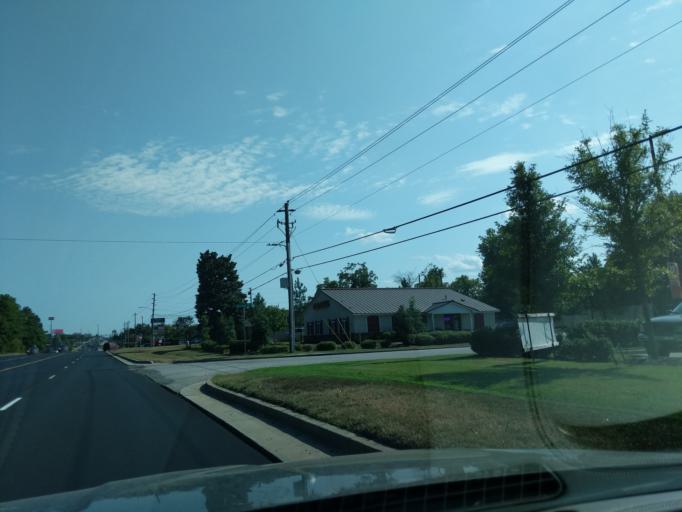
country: US
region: Georgia
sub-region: Columbia County
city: Evans
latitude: 33.4909
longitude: -82.1366
